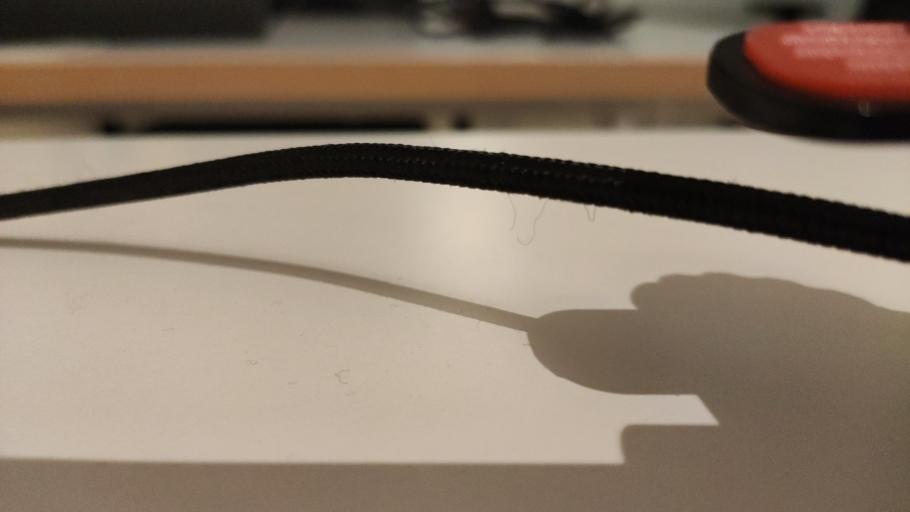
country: RU
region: Moskovskaya
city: Kurovskoye
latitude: 55.5783
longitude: 38.8885
